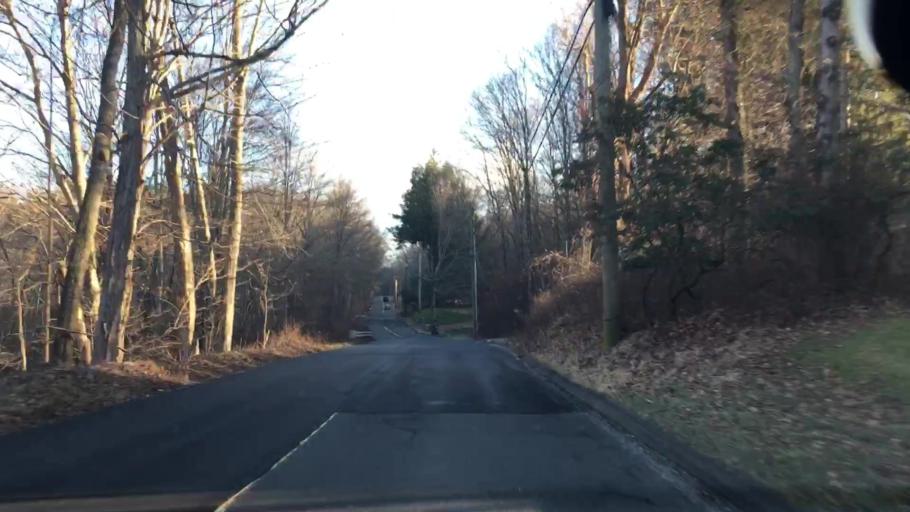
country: US
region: Connecticut
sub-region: Fairfield County
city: Newtown
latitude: 41.4521
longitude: -73.3238
